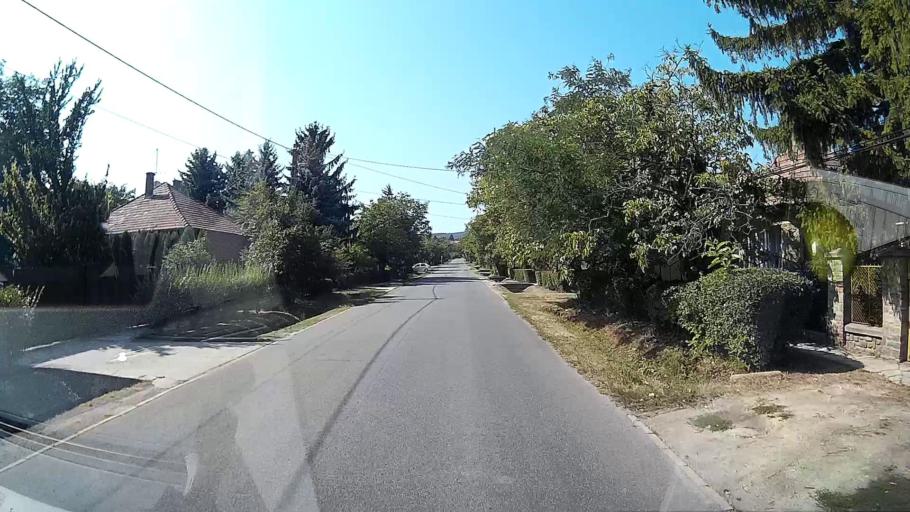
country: HU
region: Pest
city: Pomaz
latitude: 47.6412
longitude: 19.0287
